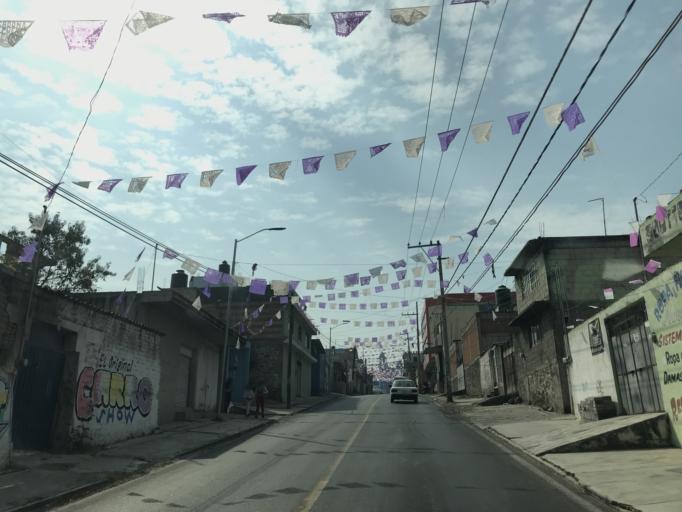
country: MX
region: Tlaxcala
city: Tenancingo
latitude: 19.1490
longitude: -98.2033
